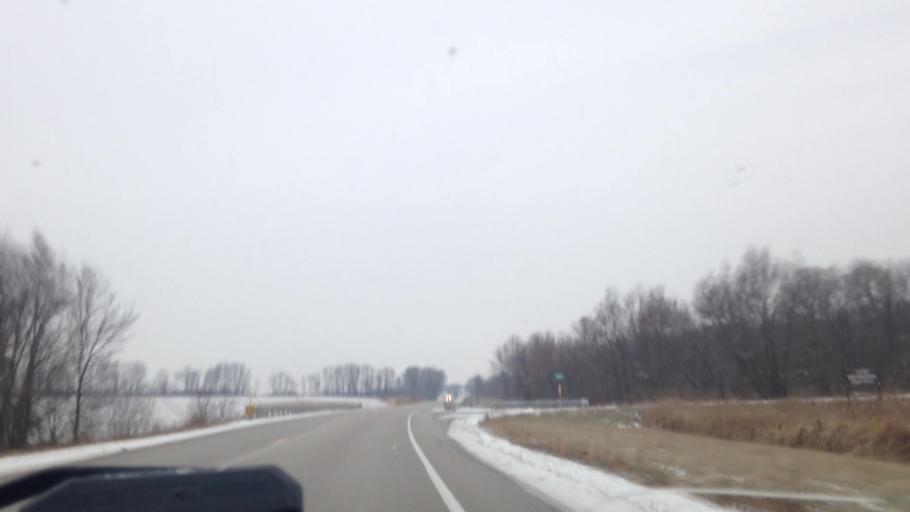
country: US
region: Wisconsin
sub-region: Dodge County
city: Hustisford
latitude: 43.3342
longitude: -88.5150
